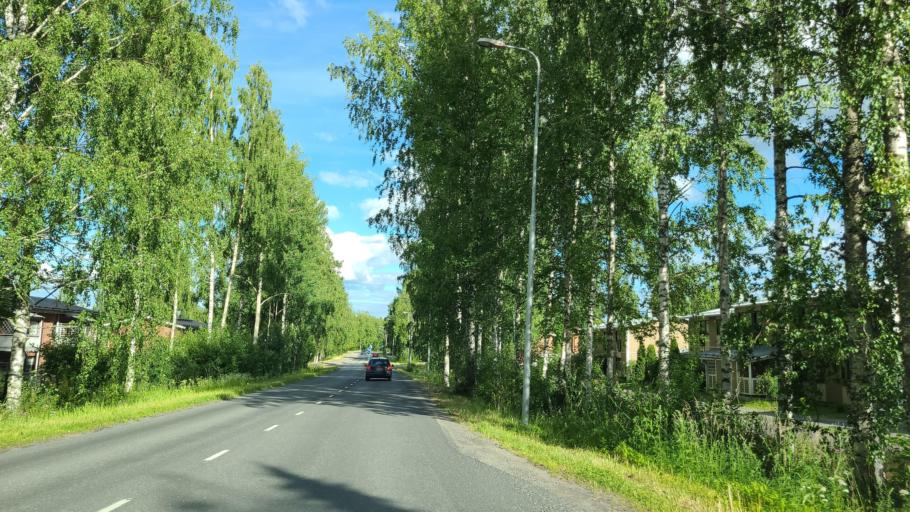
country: FI
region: Northern Savo
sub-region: Kuopio
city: Kuopio
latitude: 62.9379
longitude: 27.6502
